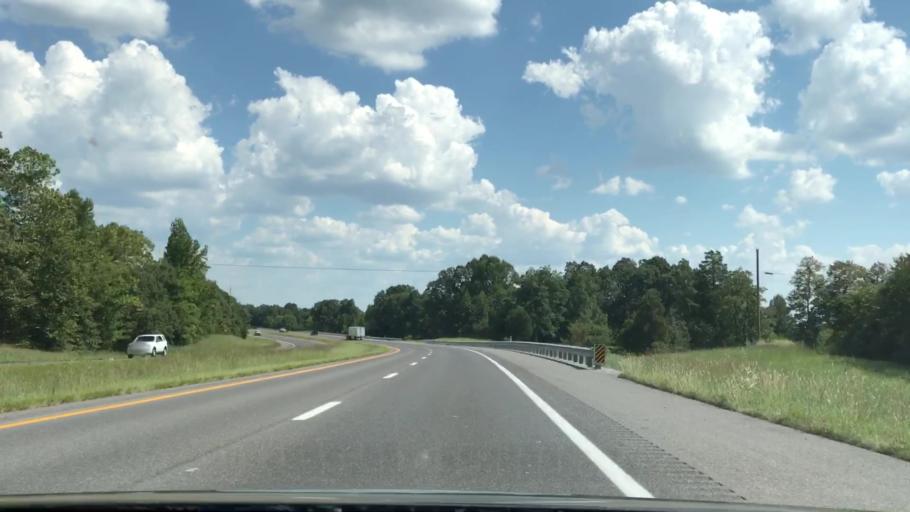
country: US
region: Kentucky
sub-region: Lyon County
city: Eddyville
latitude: 37.1067
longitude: -87.9885
